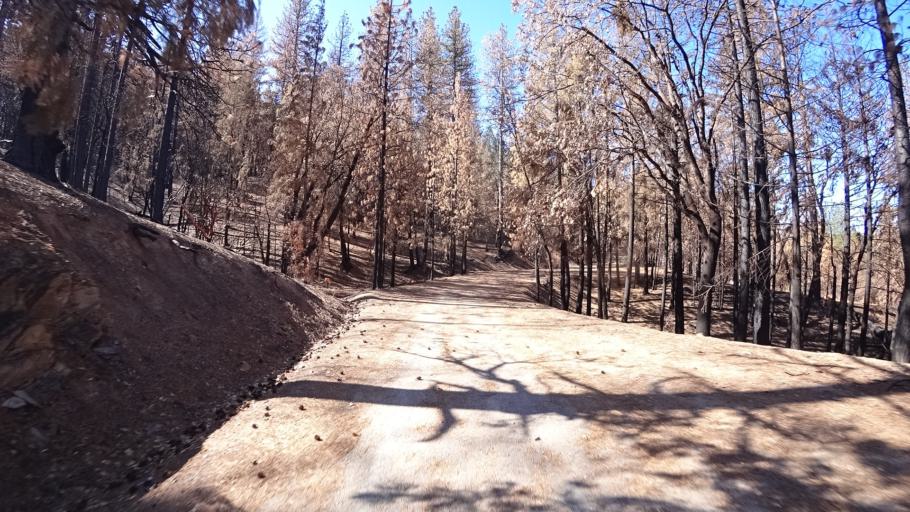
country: US
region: California
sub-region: Tehama County
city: Rancho Tehama Reserve
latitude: 39.6562
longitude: -122.7207
